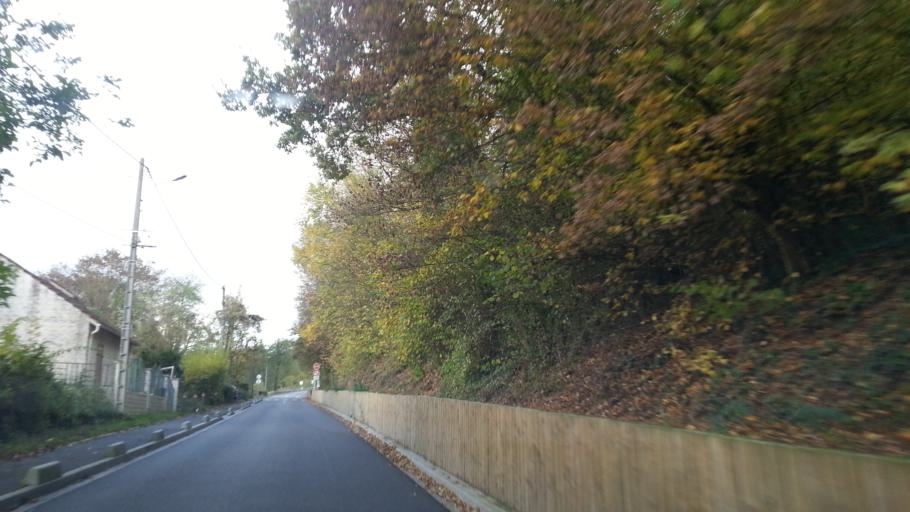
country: FR
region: Picardie
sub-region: Departement de l'Oise
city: Thiverny
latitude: 49.2534
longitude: 2.4031
